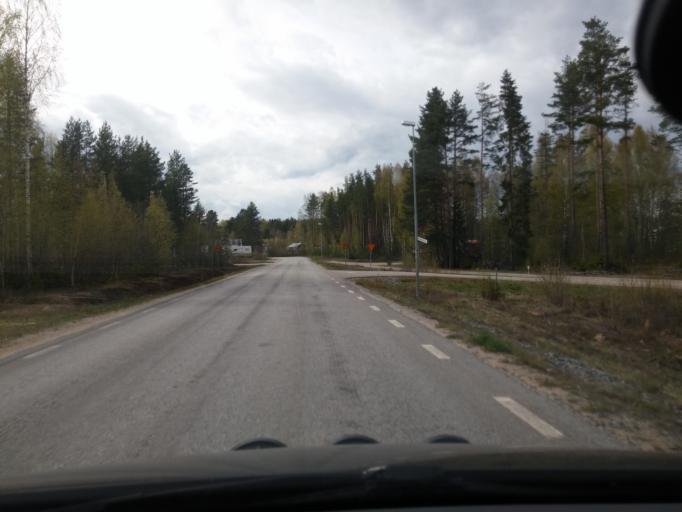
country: SE
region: Gaevleborg
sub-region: Ljusdals Kommun
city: Farila
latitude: 61.7995
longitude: 15.9068
